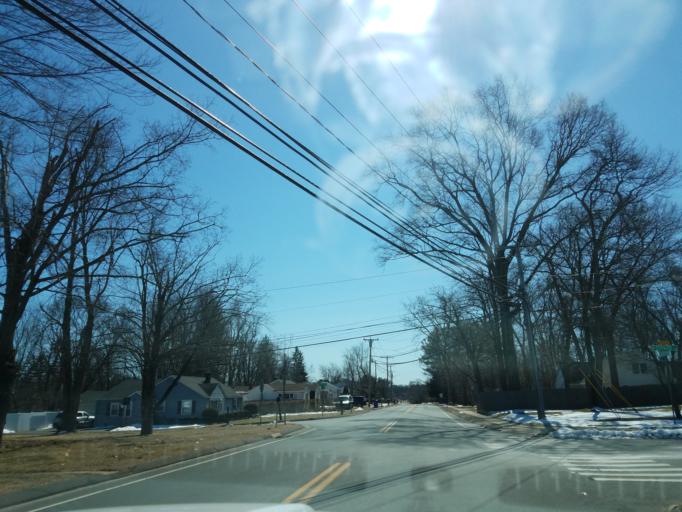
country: US
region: Connecticut
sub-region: Hartford County
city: Windsor Locks
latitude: 41.9116
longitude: -72.6370
